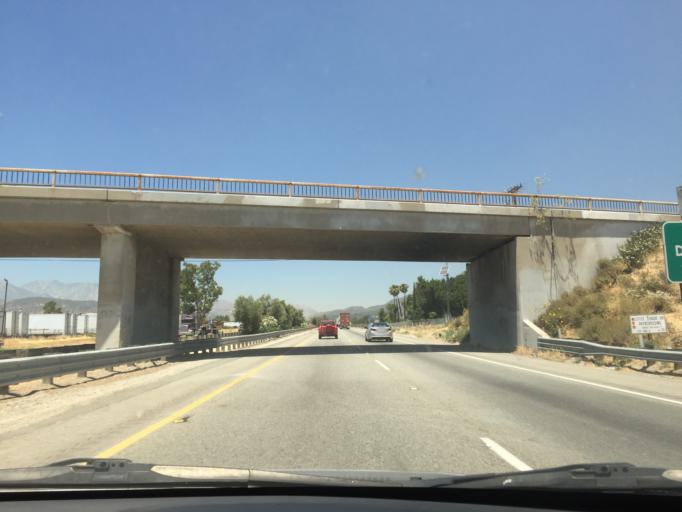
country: US
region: California
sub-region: San Bernardino County
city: Muscoy
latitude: 34.1990
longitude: -117.3717
